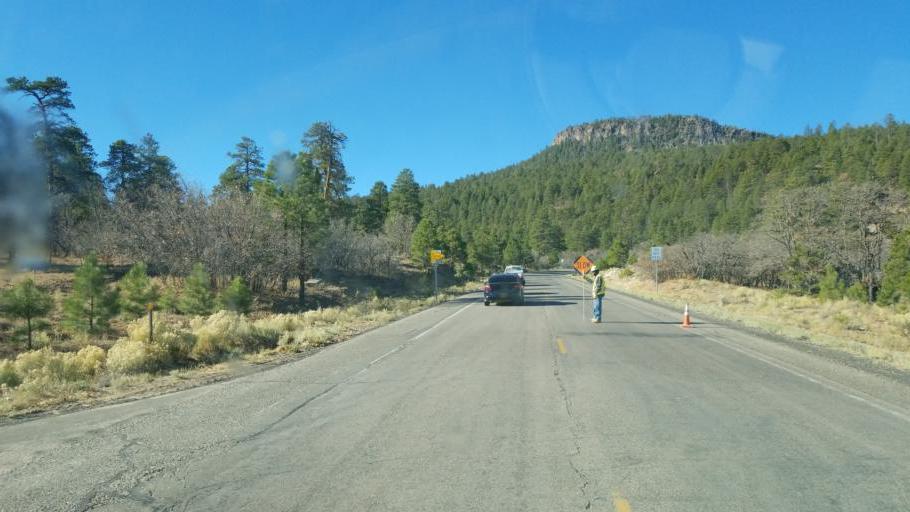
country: US
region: New Mexico
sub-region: McKinley County
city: Navajo
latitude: 36.0952
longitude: -108.8364
